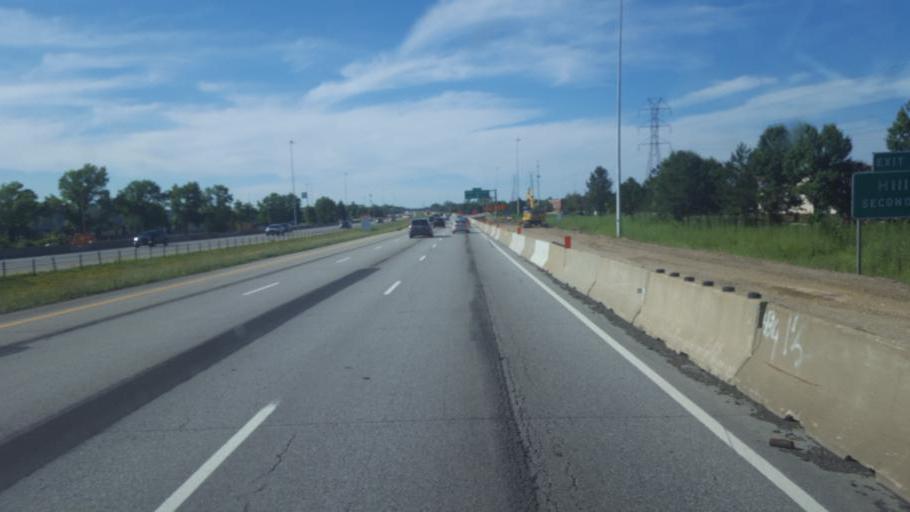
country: US
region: Ohio
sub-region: Franklin County
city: Hilliard
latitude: 40.0270
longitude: -83.1222
